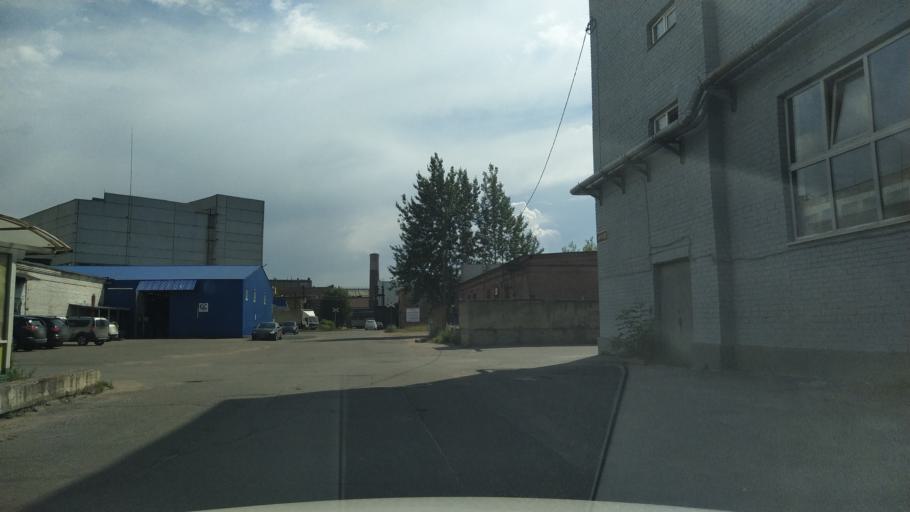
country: RU
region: Leningrad
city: Finlyandskiy
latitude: 59.9631
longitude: 30.3647
